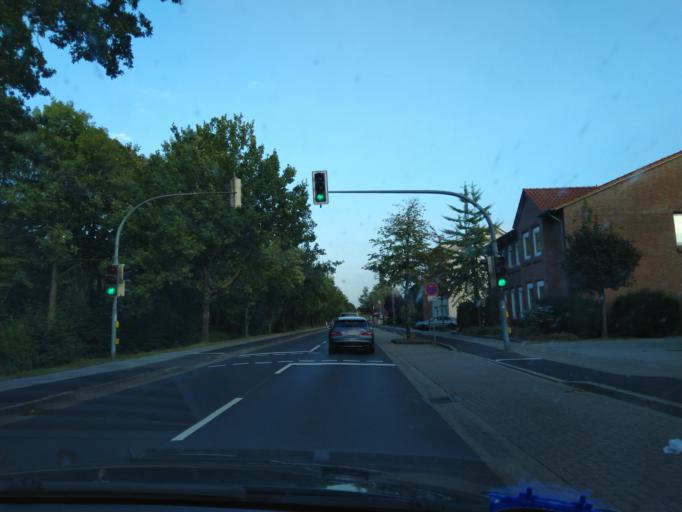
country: DE
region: Lower Saxony
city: Papenburg
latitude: 53.0759
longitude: 7.4070
